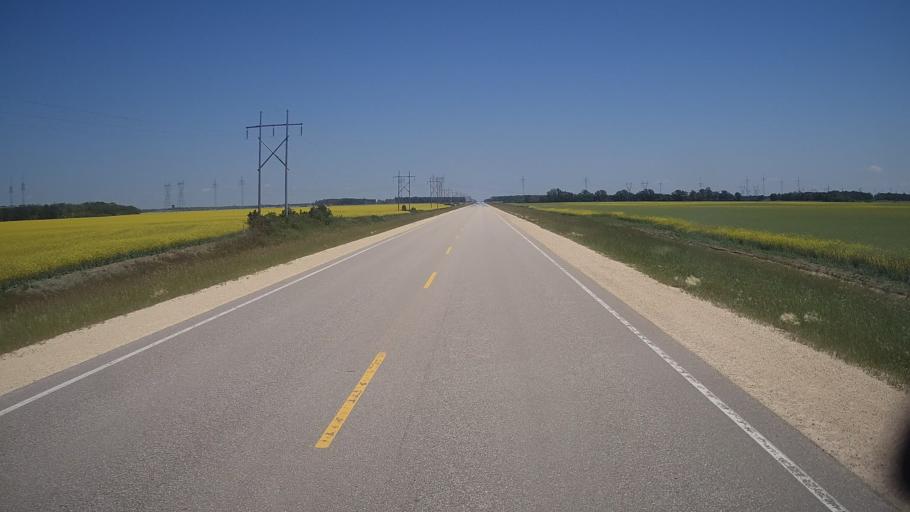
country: CA
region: Manitoba
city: Stonewall
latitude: 50.1227
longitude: -97.5044
